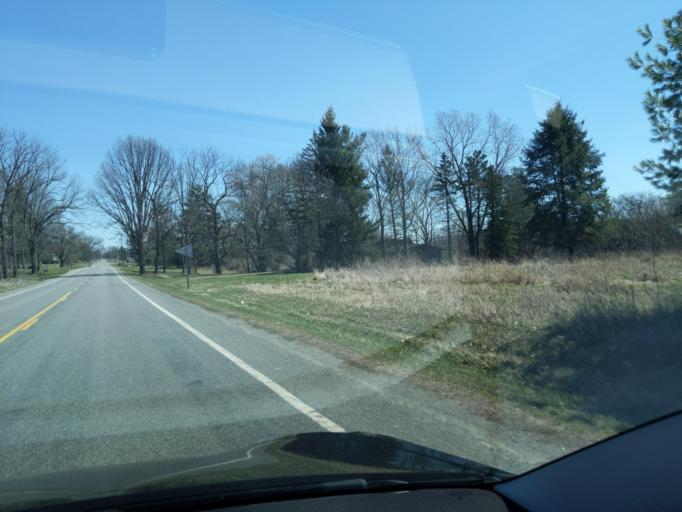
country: US
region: Michigan
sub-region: Ingham County
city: Holt
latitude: 42.5821
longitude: -84.5587
